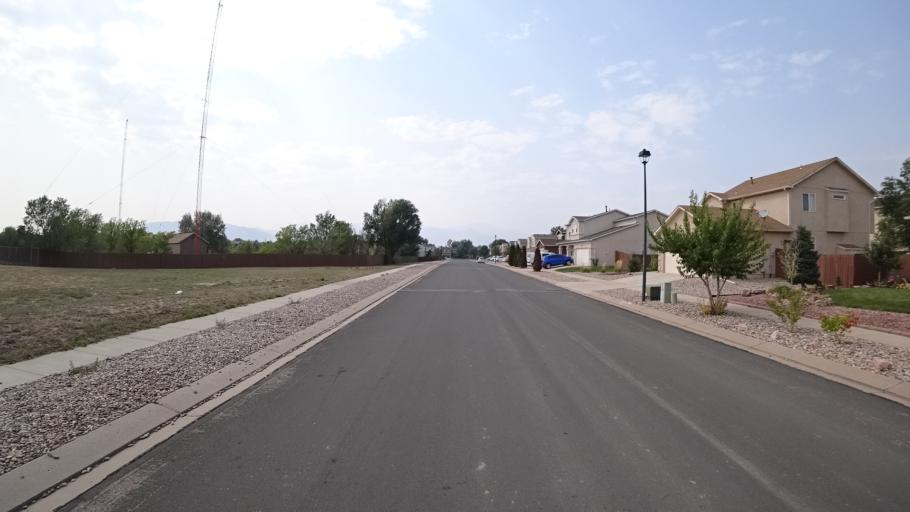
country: US
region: Colorado
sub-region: El Paso County
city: Cimarron Hills
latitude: 38.8269
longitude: -104.7412
